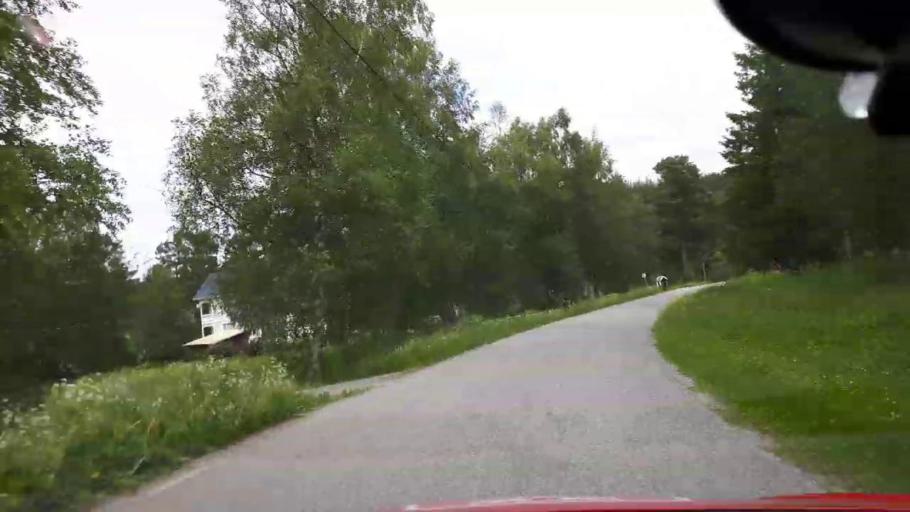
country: SE
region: Jaemtland
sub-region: Braecke Kommun
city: Braecke
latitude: 62.8848
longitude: 15.2722
